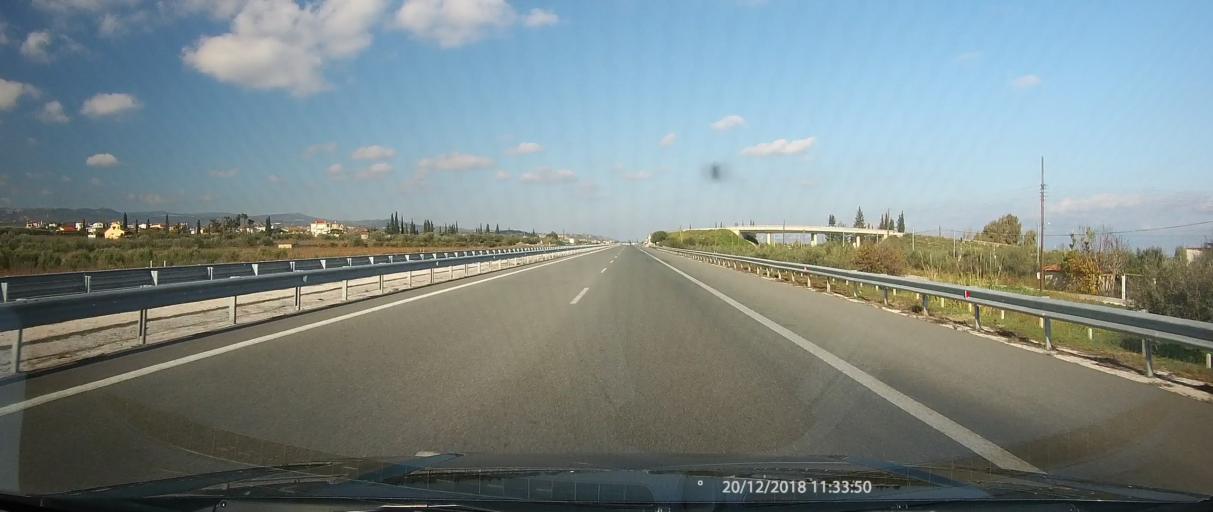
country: GR
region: Peloponnese
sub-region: Nomos Korinthias
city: Velo
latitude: 37.9502
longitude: 22.7556
